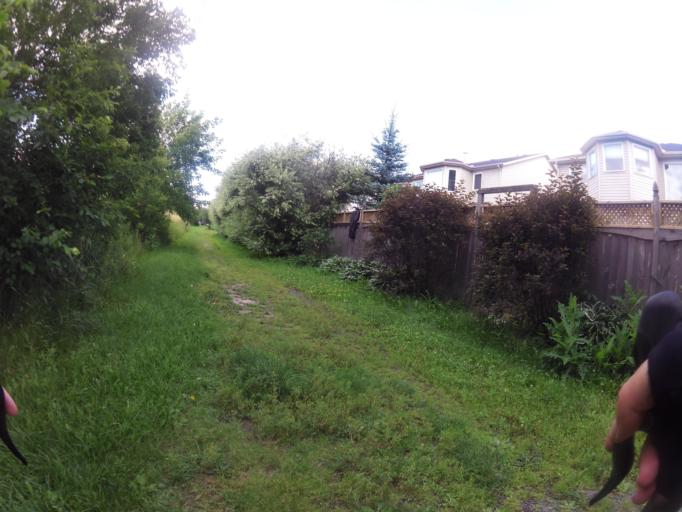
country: CA
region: Ontario
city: Ottawa
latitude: 45.2864
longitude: -75.6904
